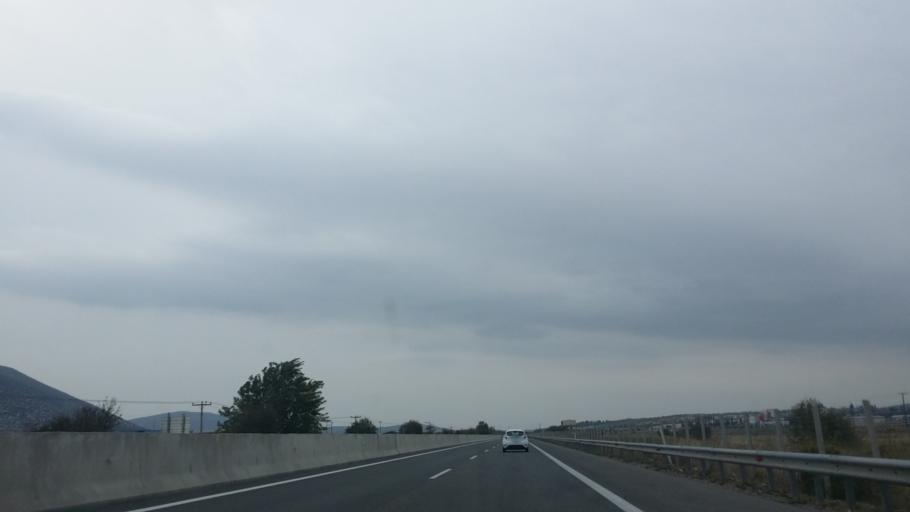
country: GR
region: Central Greece
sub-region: Nomos Voiotias
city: Arma
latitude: 38.3717
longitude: 23.3977
